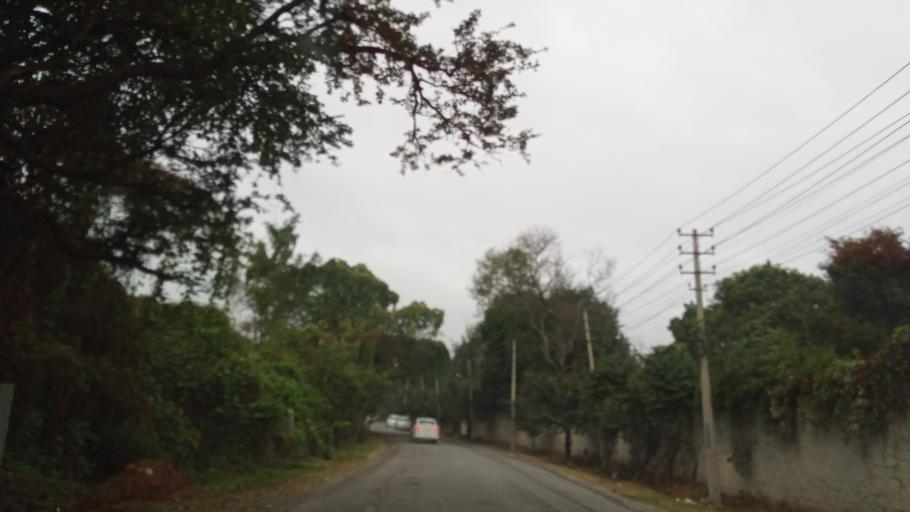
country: IN
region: Karnataka
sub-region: Bangalore Urban
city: Bangalore
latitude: 12.9084
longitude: 77.4963
